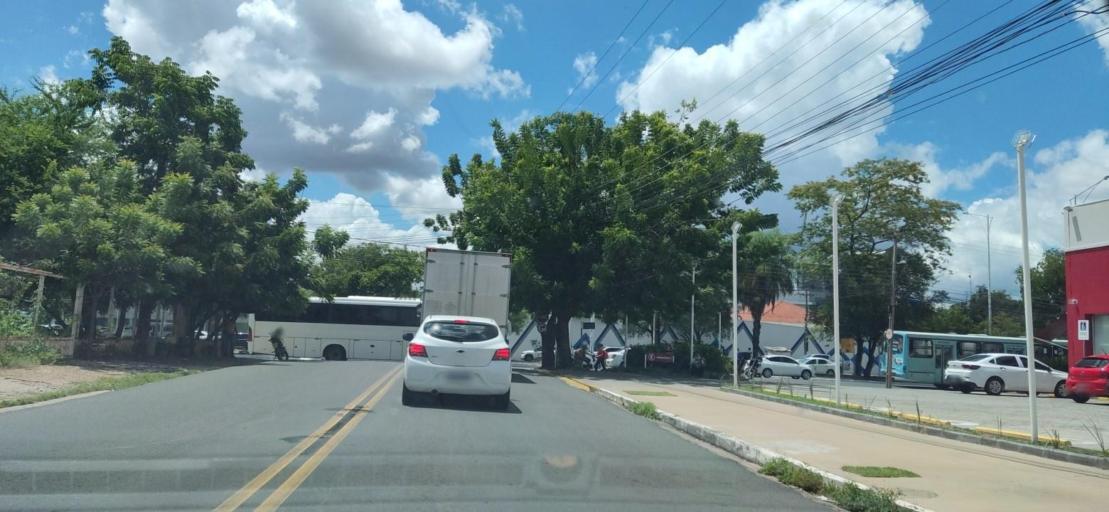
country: BR
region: Piaui
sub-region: Teresina
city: Teresina
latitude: -5.0852
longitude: -42.7993
